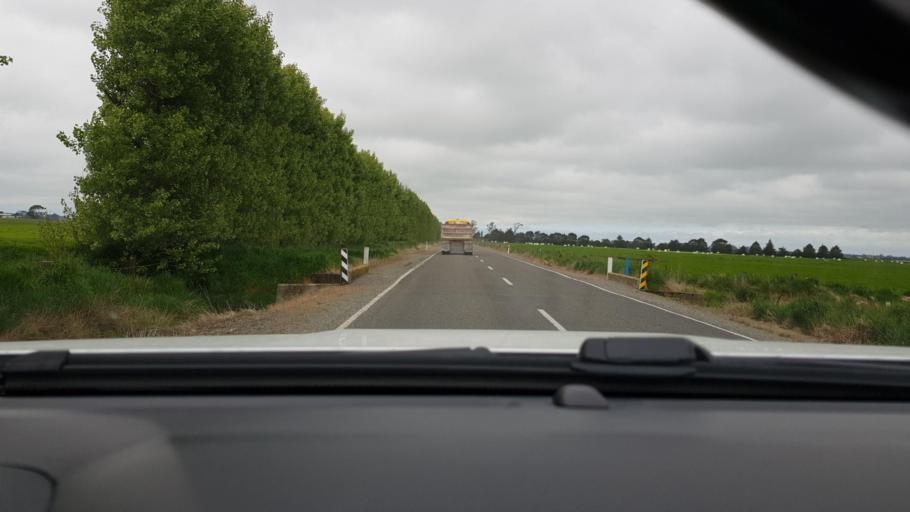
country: NZ
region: Otago
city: Oamaru
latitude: -44.9648
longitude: 170.9496
